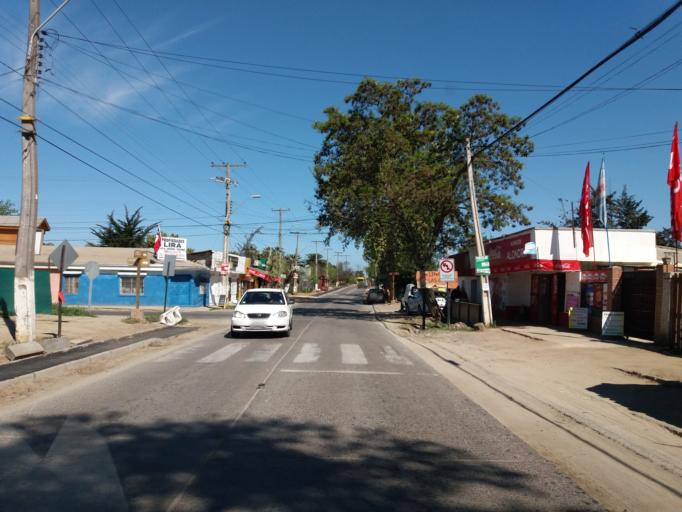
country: CL
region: Valparaiso
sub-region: Provincia de Marga Marga
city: Limache
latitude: -33.0006
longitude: -71.1995
